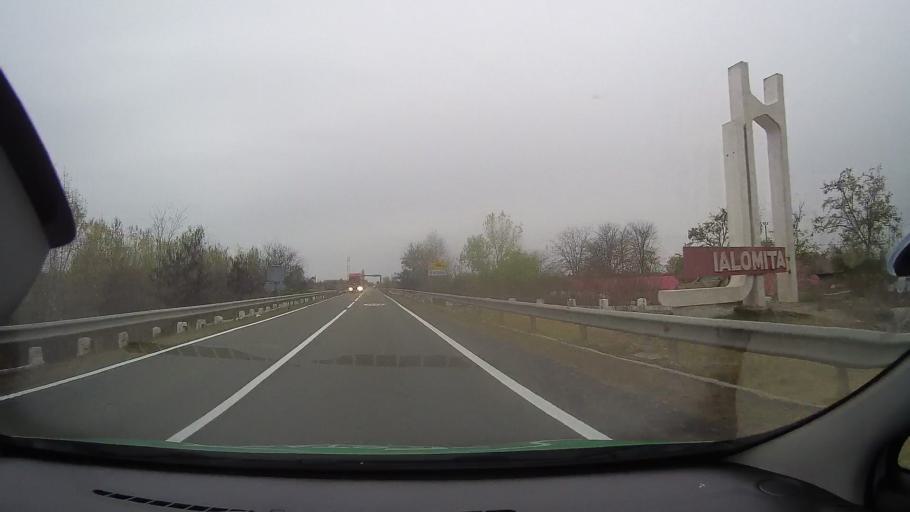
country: RO
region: Ialomita
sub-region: Comuna Giurgeni
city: Giurgeni
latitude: 44.7521
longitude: 27.8575
